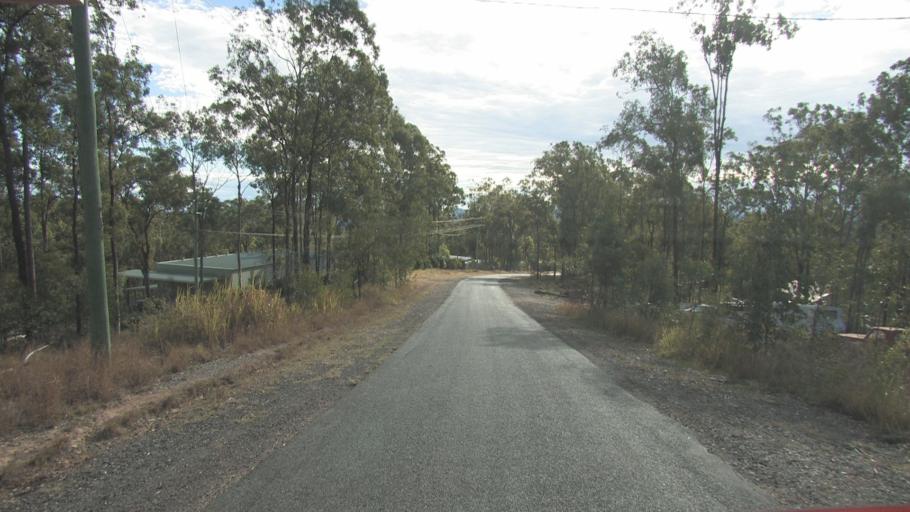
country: AU
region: Queensland
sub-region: Logan
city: Cedar Vale
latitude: -27.8462
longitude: 153.0727
